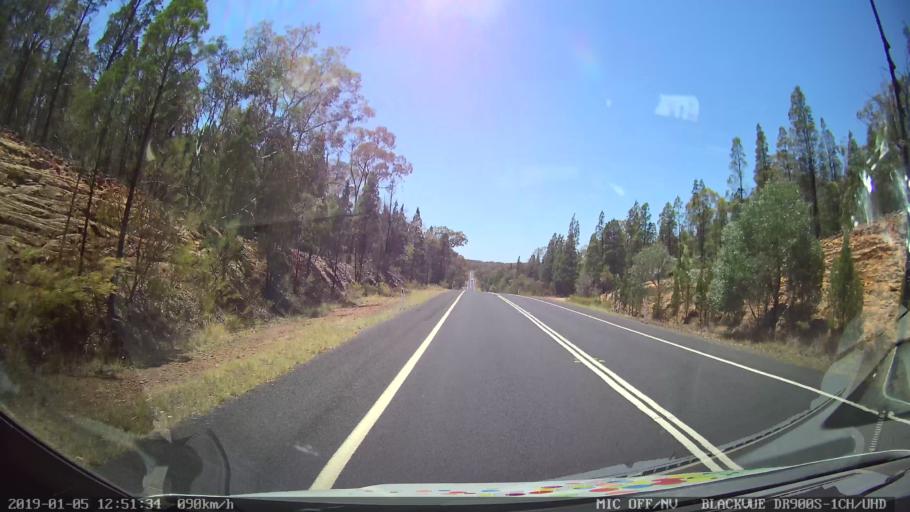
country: AU
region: New South Wales
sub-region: Warrumbungle Shire
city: Coonabarabran
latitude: -31.1211
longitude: 149.6415
